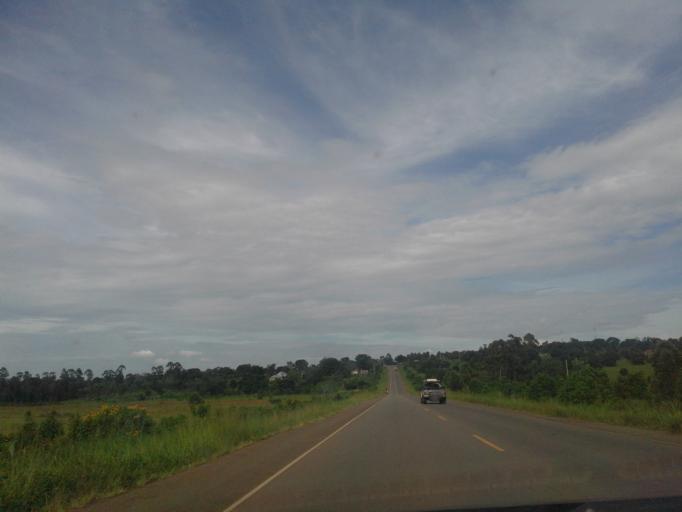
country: UG
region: Central Region
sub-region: Lwengo District
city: Lwengo
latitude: -0.3627
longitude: 31.5417
